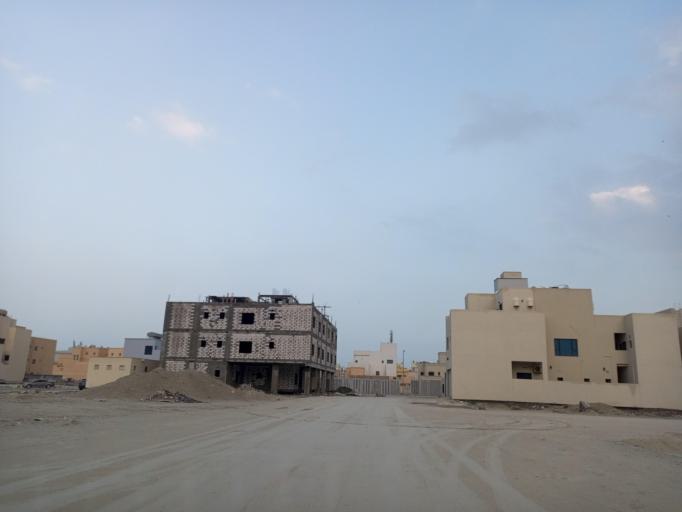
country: BH
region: Muharraq
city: Al Hadd
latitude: 26.2368
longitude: 50.6470
